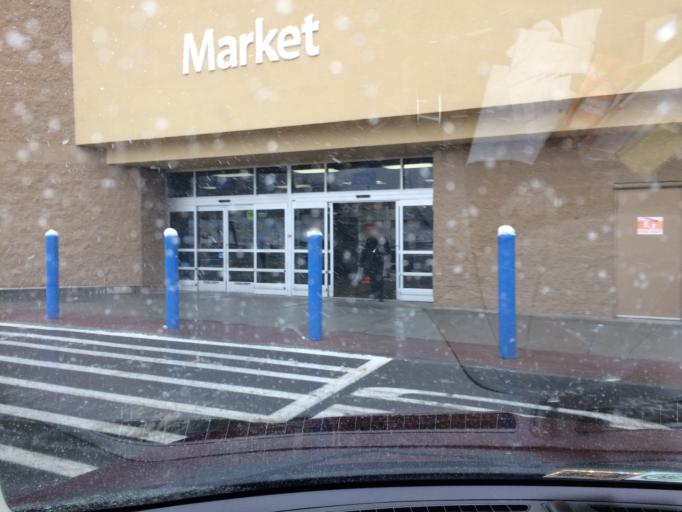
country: US
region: Virginia
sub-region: Amherst County
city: Madison Heights
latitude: 37.4617
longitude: -79.1163
